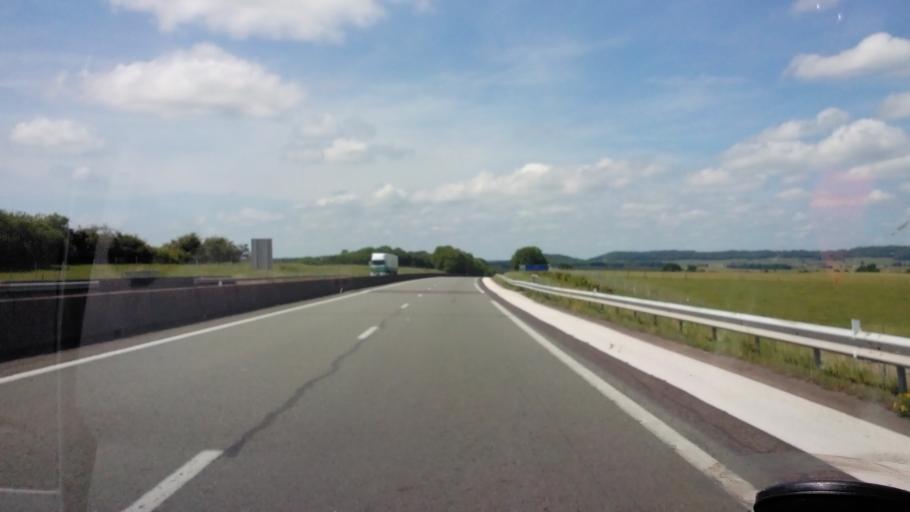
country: FR
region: Champagne-Ardenne
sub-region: Departement de la Haute-Marne
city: Saulxures
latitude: 48.0830
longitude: 5.6264
